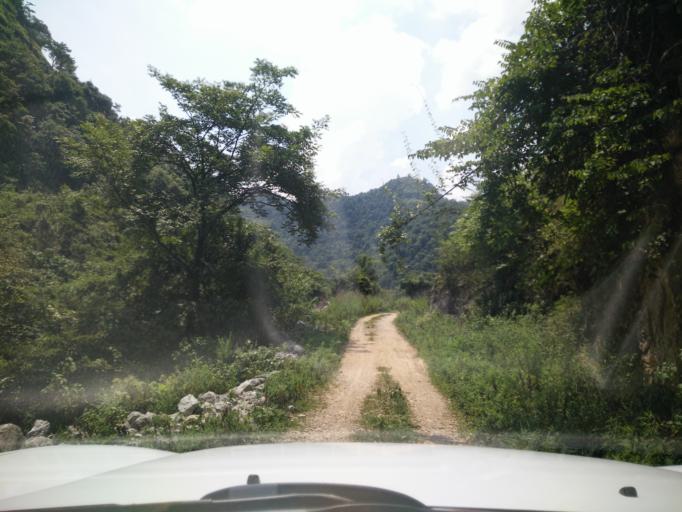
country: CN
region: Guangxi Zhuangzu Zizhiqu
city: Xinzhou
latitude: 25.0131
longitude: 105.7055
